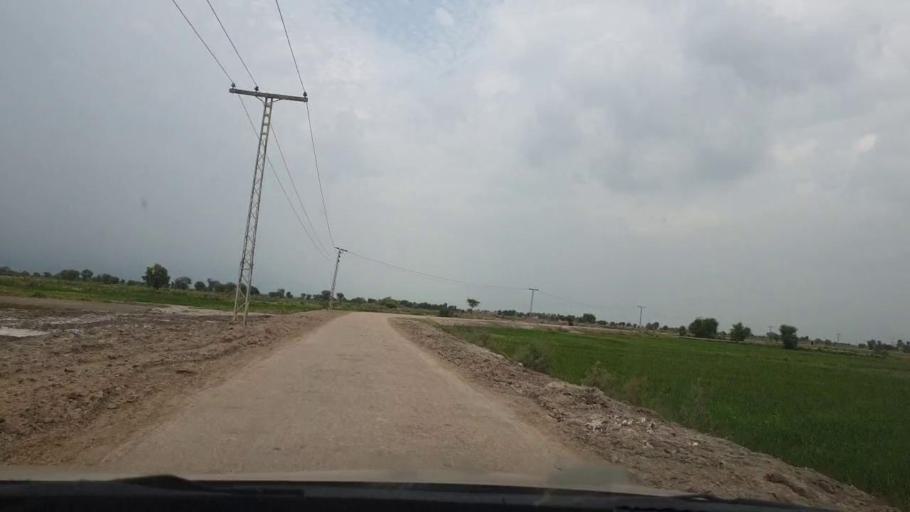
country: PK
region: Sindh
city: Ratodero
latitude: 27.8120
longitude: 68.3083
